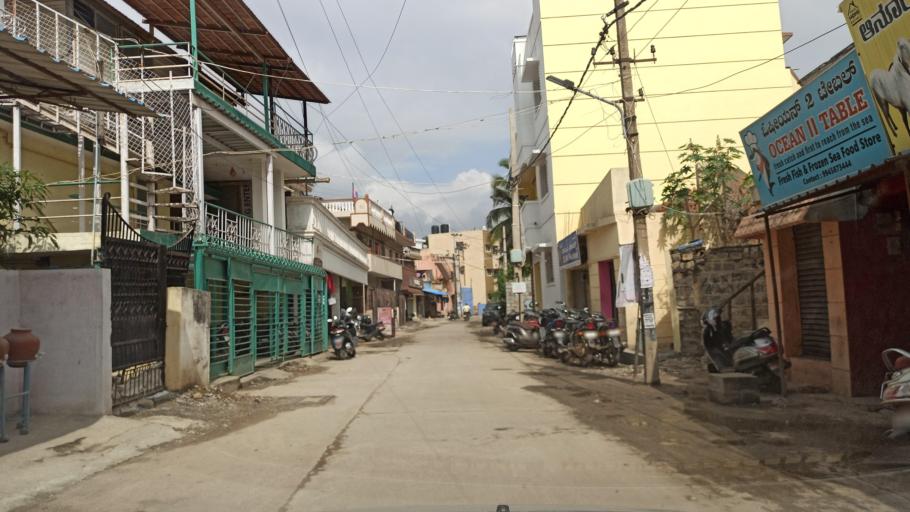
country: IN
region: Karnataka
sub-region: Bangalore Urban
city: Bangalore
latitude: 13.0067
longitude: 77.6744
